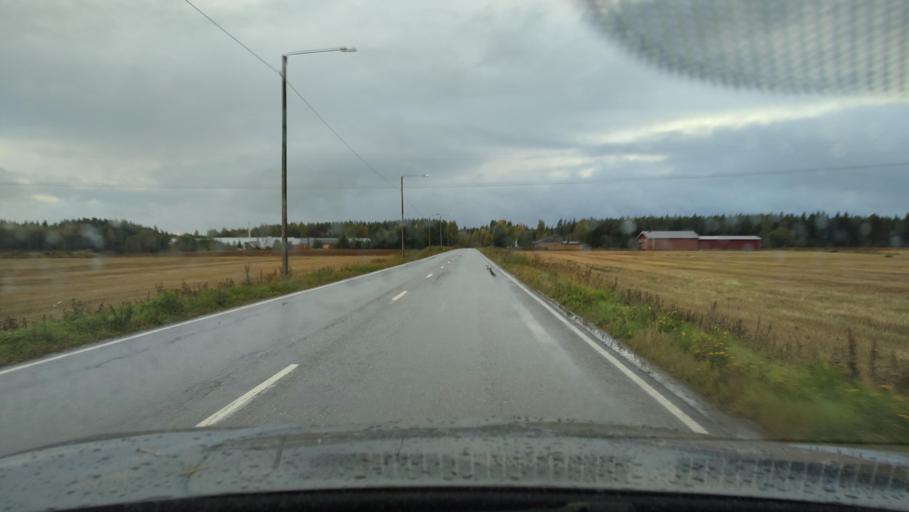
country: FI
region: Southern Ostrobothnia
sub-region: Suupohja
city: Karijoki
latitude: 62.2374
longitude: 21.6100
